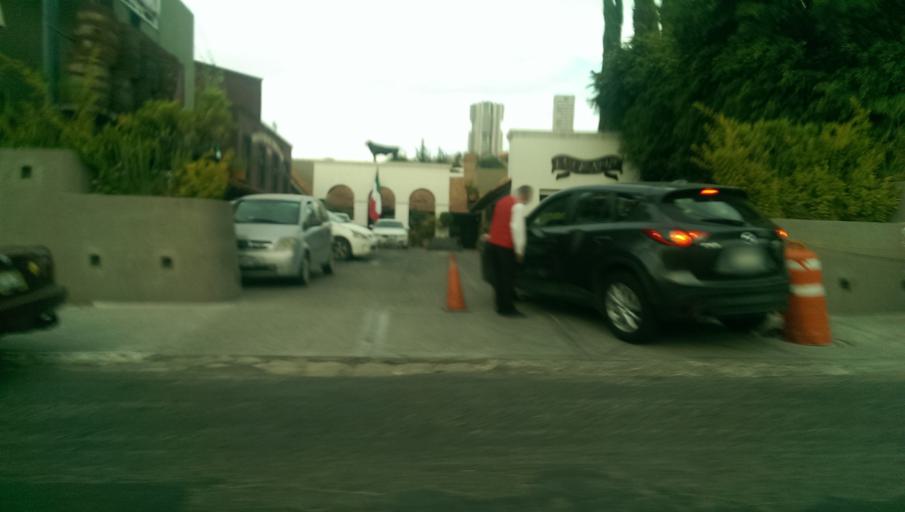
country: MX
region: Queretaro
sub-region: Queretaro
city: Santiago de Queretaro
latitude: 20.5952
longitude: -100.3706
